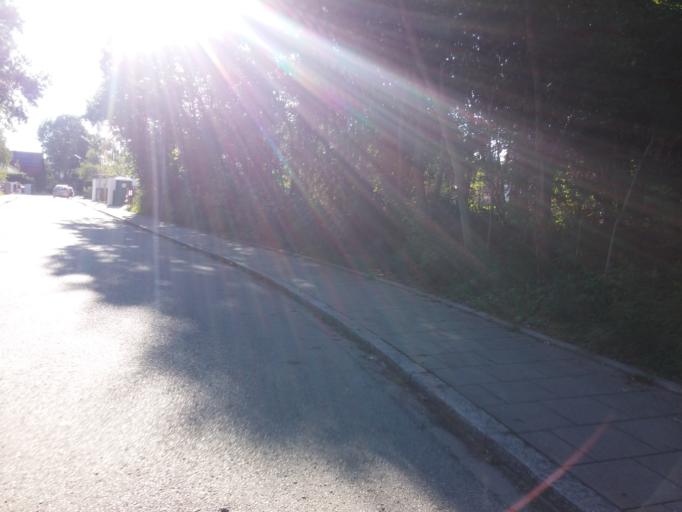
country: DE
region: Bavaria
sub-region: Upper Bavaria
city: Zorneding
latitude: 48.0988
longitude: 11.8012
